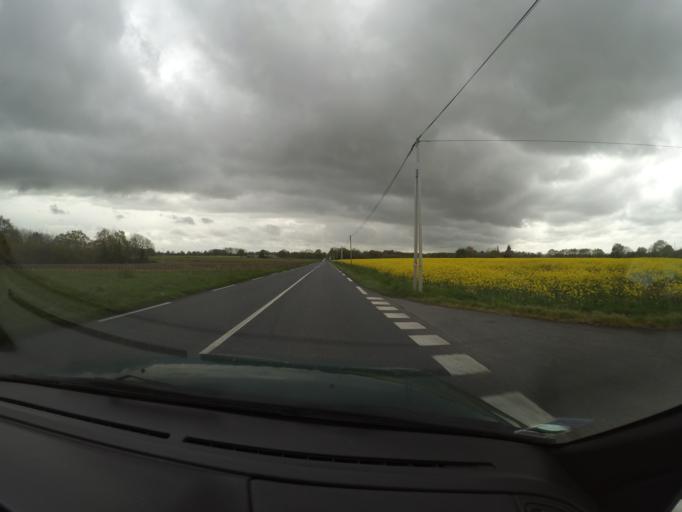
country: FR
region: Pays de la Loire
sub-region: Departement de la Loire-Atlantique
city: La Remaudiere
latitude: 47.2068
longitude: -1.2422
